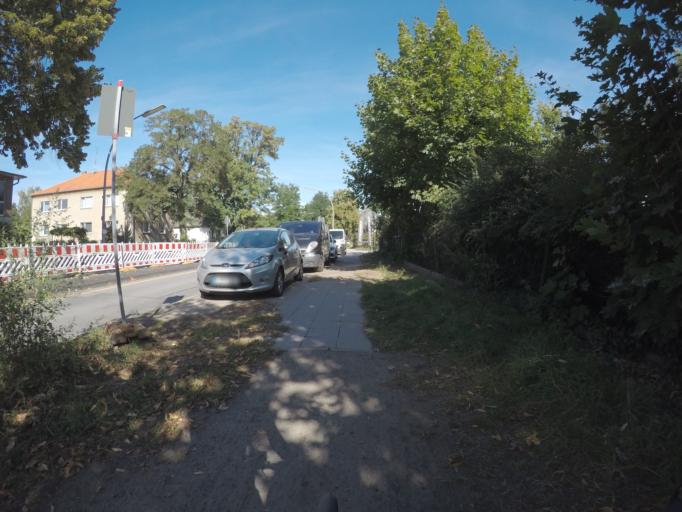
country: DE
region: Berlin
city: Heiligensee
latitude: 52.6170
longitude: 13.2207
